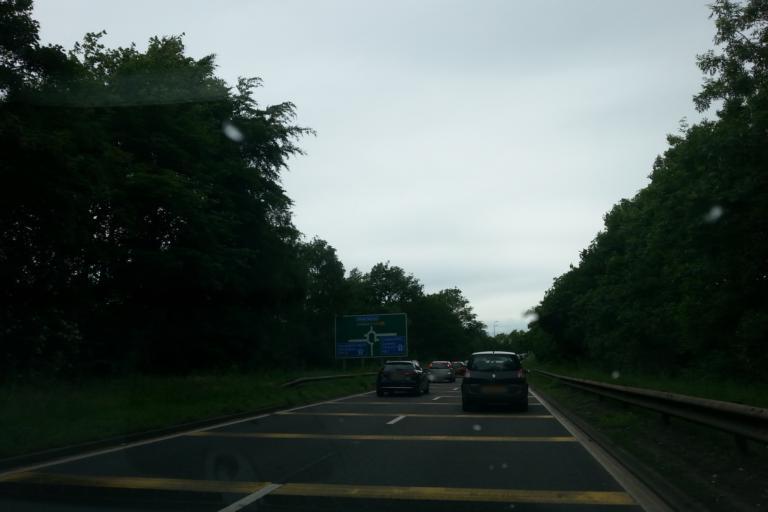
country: GB
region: England
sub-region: Solihull
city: Chelmsley Wood
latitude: 52.4733
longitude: -1.7068
